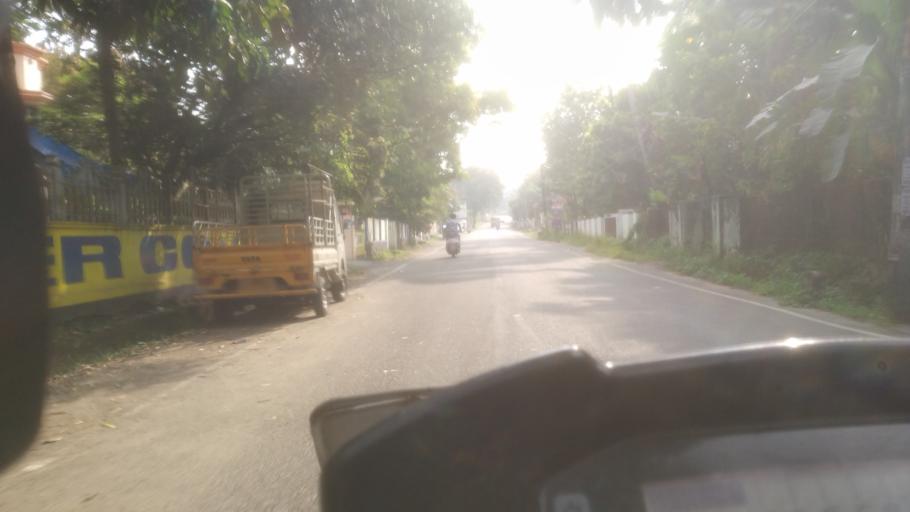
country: IN
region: Kerala
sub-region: Ernakulam
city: Angamali
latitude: 10.1624
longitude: 76.3702
